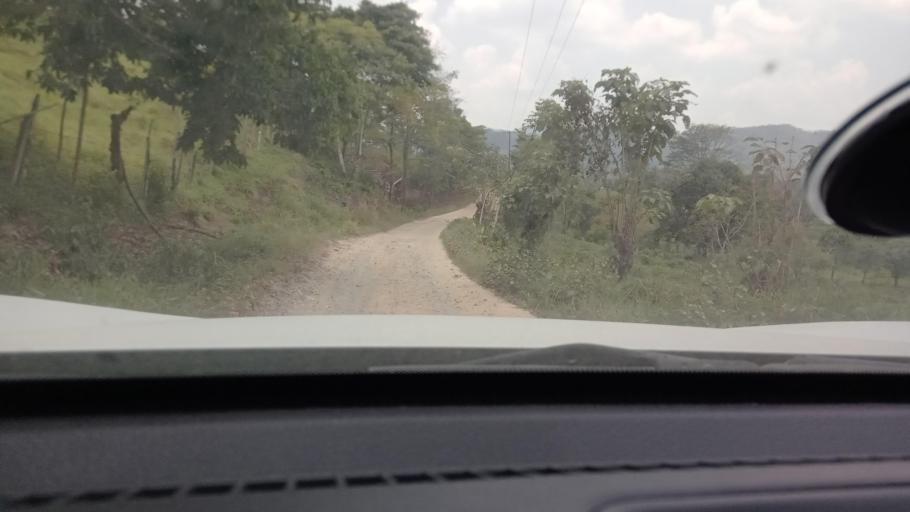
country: MX
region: Tabasco
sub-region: Huimanguillo
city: Francisco Rueda
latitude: 17.5187
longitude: -93.8882
